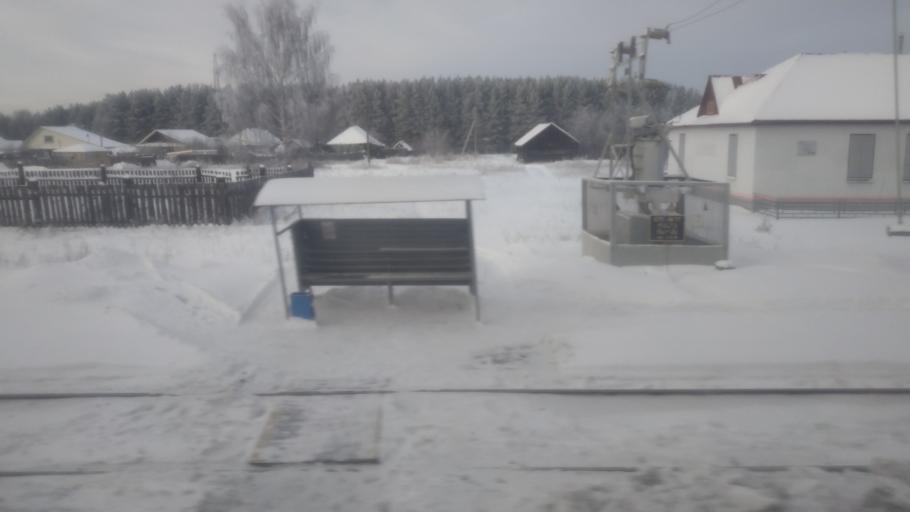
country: RU
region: Udmurtiya
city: Kizner
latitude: 56.3877
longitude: 51.7185
